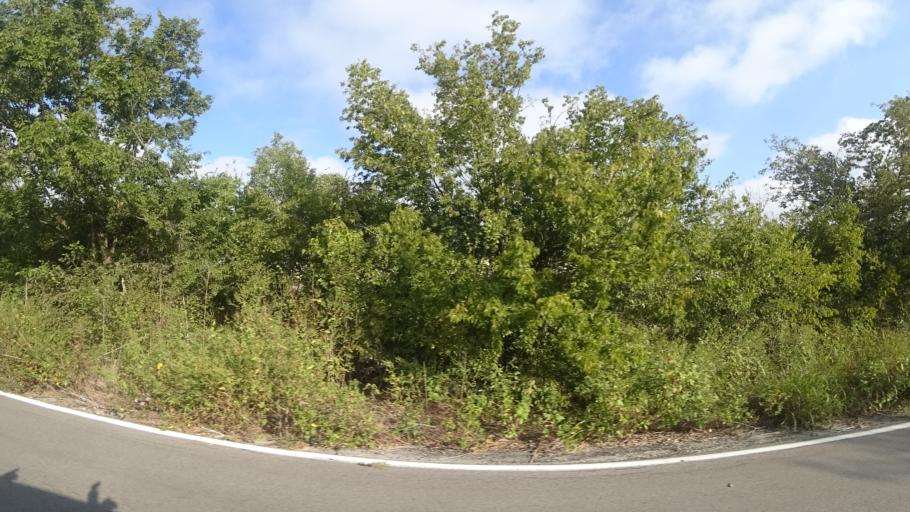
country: US
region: Texas
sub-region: Travis County
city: Manor
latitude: 30.3656
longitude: -97.6182
